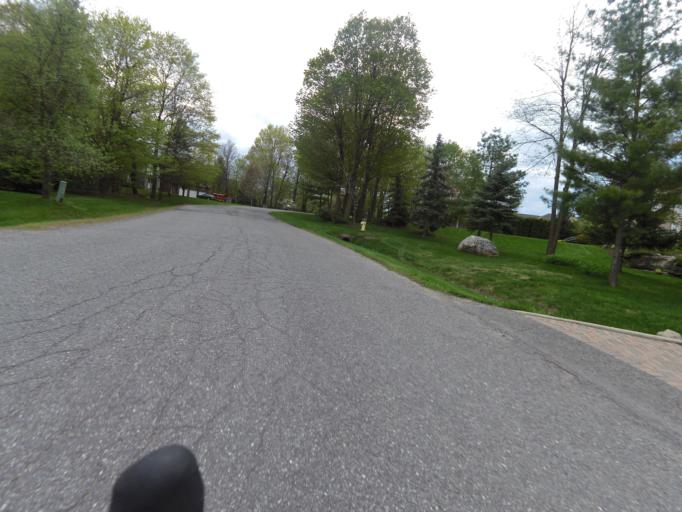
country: CA
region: Ontario
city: Bells Corners
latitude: 45.2837
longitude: -75.7881
